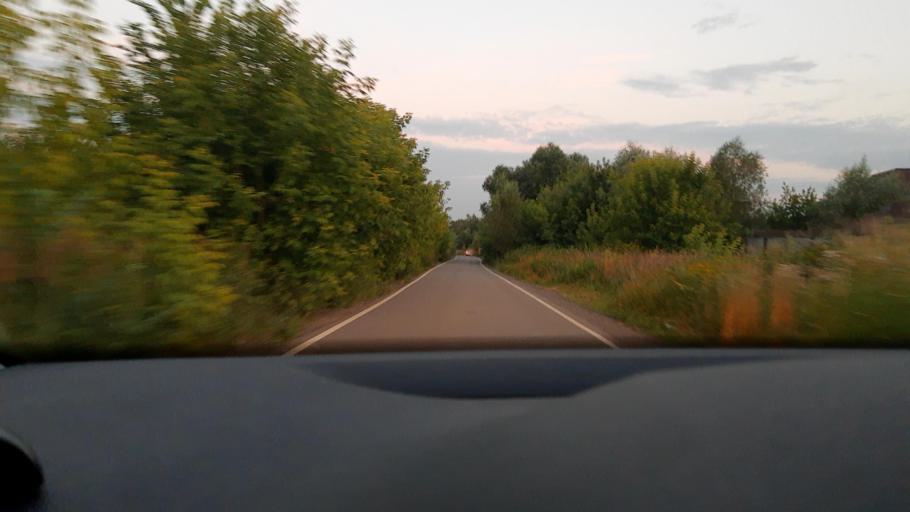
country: RU
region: Moskovskaya
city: Novopodrezkovo
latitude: 55.9123
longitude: 37.3672
